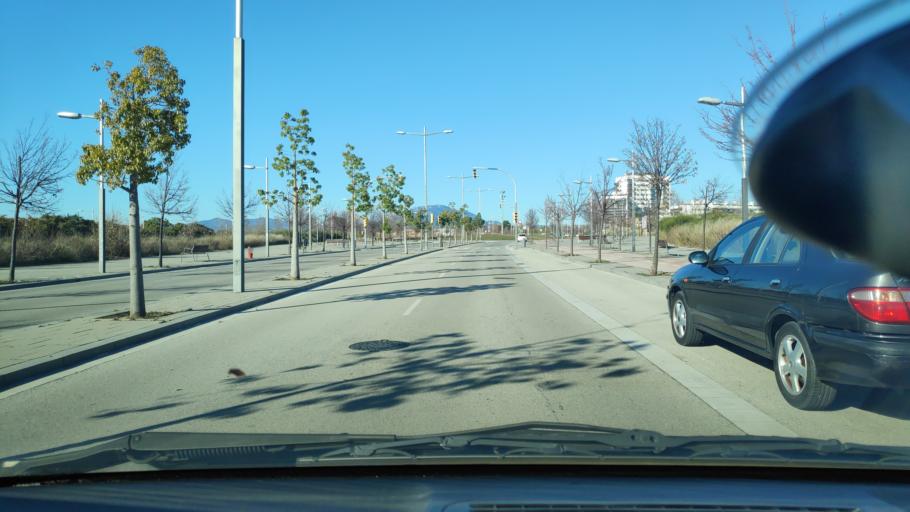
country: ES
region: Catalonia
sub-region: Provincia de Barcelona
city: Sant Quirze del Valles
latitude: 41.5458
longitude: 2.0799
